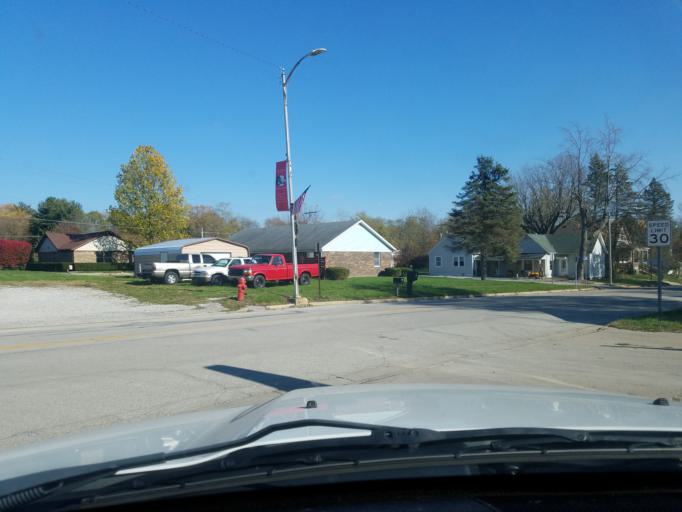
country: US
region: Indiana
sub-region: Hendricks County
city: Pittsboro
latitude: 39.9254
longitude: -86.6269
